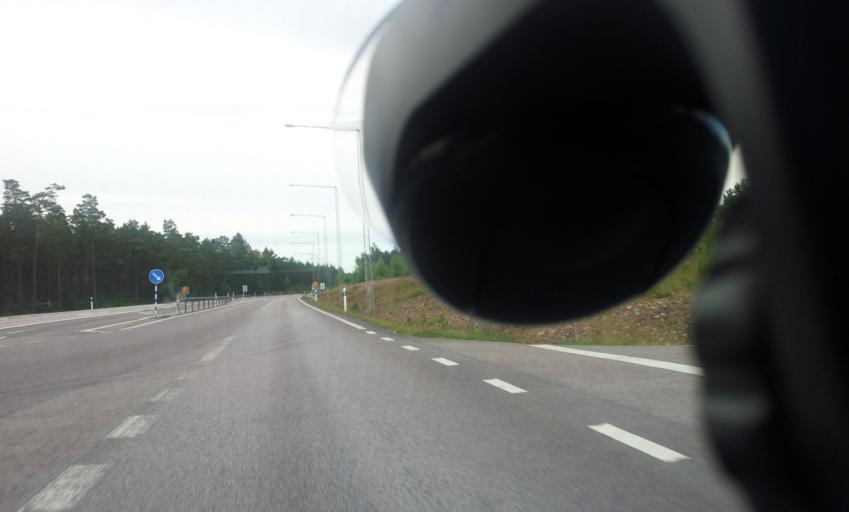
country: SE
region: Kalmar
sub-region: Monsteras Kommun
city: Moensteras
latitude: 57.0812
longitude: 16.4832
